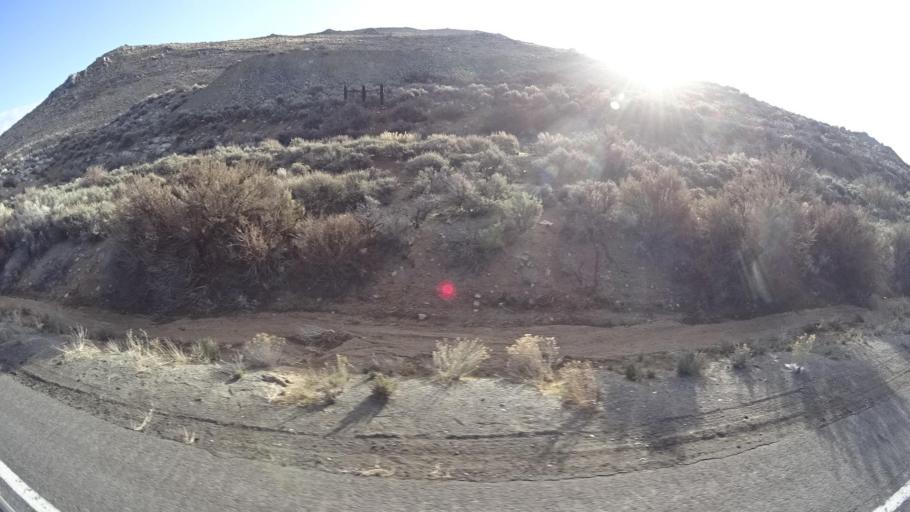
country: US
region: Nevada
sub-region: Washoe County
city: Cold Springs
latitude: 39.6479
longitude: -119.9578
